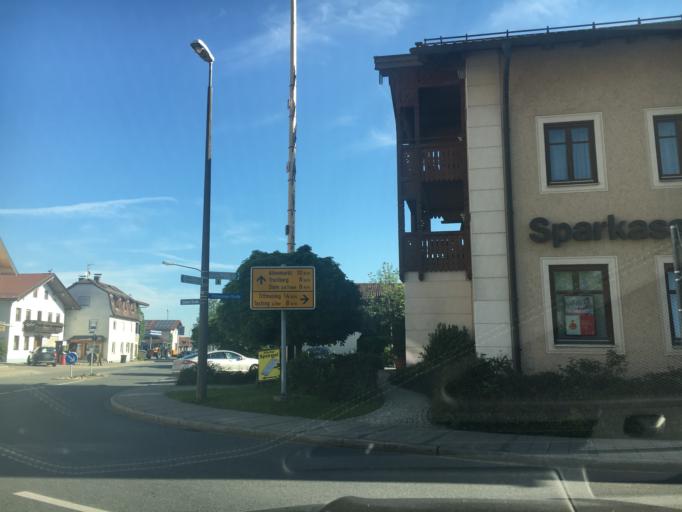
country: DE
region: Bavaria
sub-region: Upper Bavaria
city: Palling
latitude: 48.0009
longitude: 12.6371
